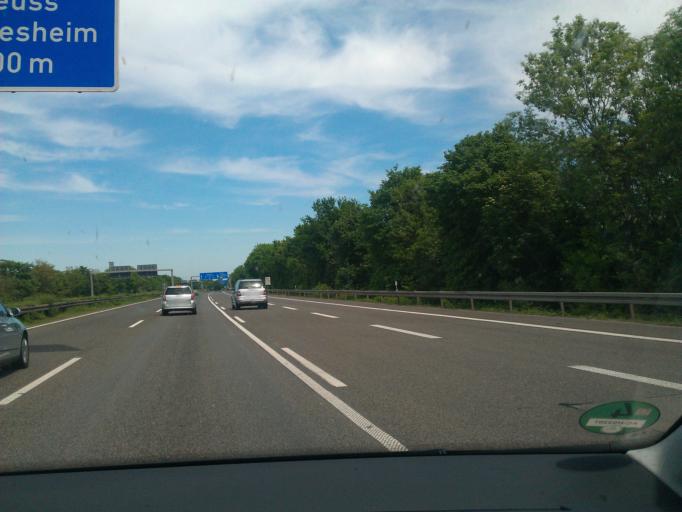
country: DE
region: North Rhine-Westphalia
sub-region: Regierungsbezirk Dusseldorf
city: Dusseldorf
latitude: 51.1586
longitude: 6.7591
